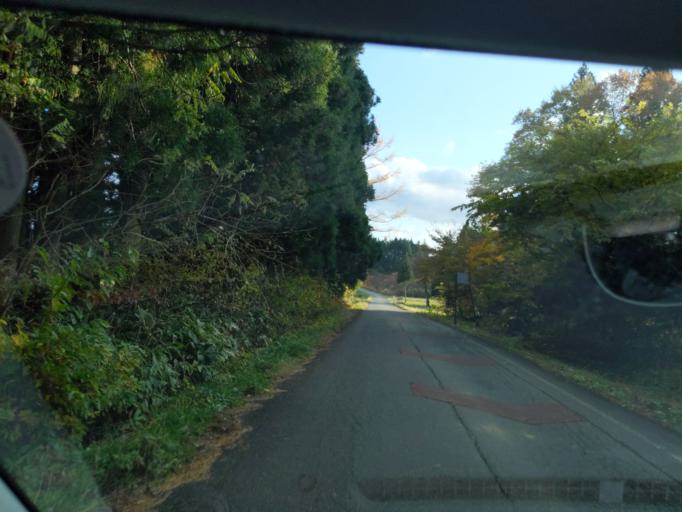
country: JP
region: Iwate
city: Mizusawa
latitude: 39.1157
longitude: 140.9999
